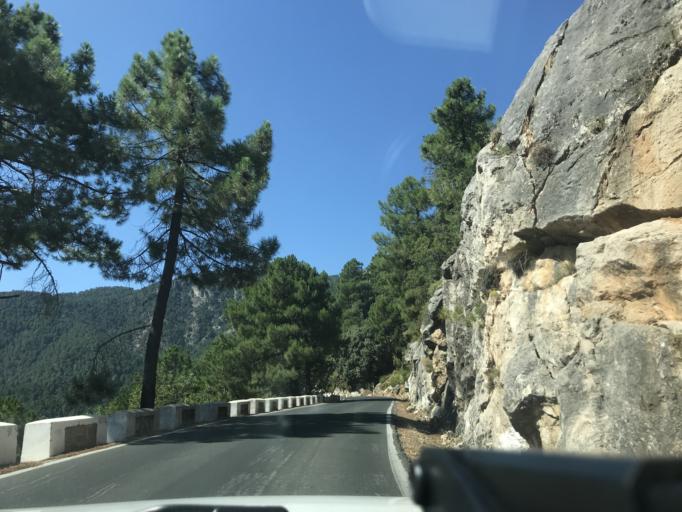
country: ES
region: Andalusia
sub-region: Provincia de Jaen
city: La Iruela
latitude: 37.9271
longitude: -2.9495
